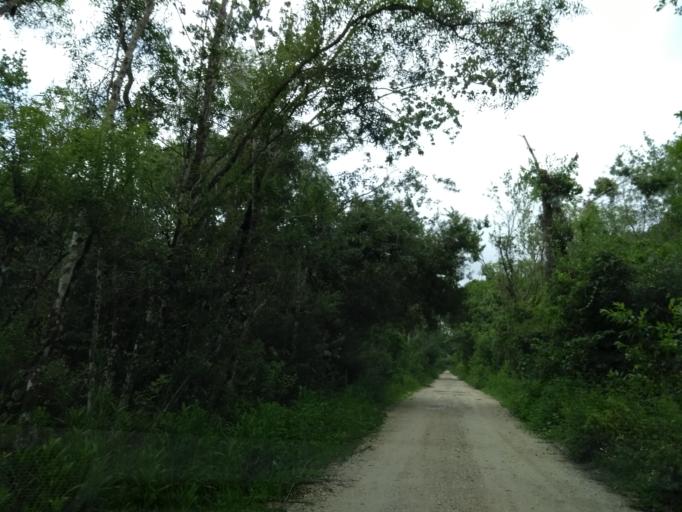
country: US
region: Florida
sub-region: Collier County
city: Lely Resort
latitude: 25.9948
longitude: -81.4111
